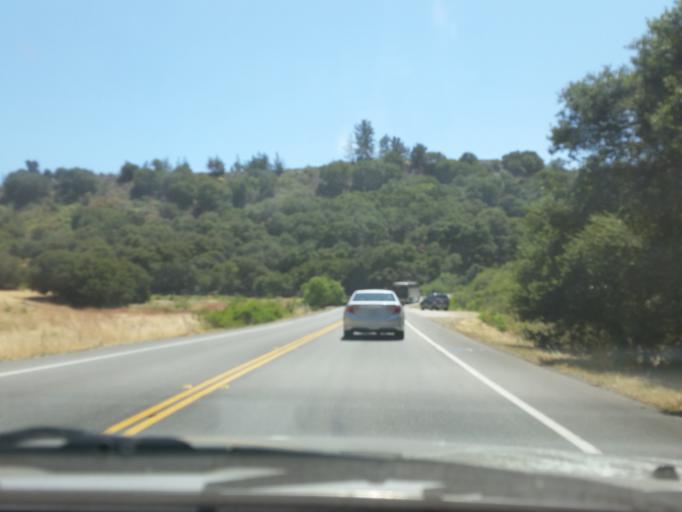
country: US
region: California
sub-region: San Luis Obispo County
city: Avila Beach
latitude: 35.1813
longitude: -120.7231
